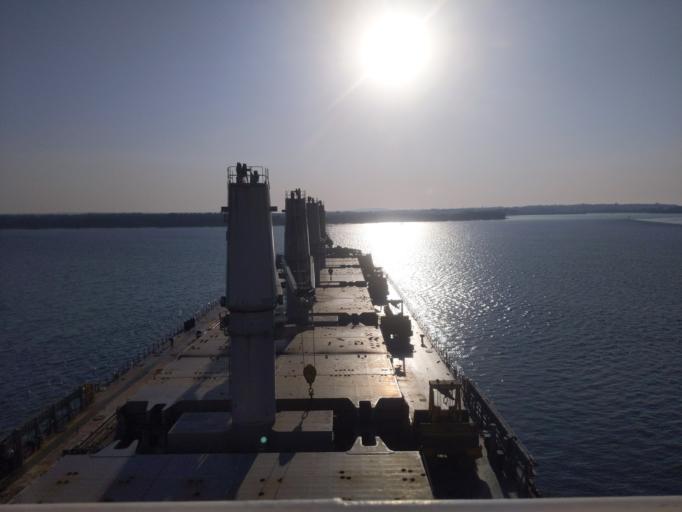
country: ZA
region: KwaZulu-Natal
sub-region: uThungulu District Municipality
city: Richards Bay
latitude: -28.8028
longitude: 32.0541
